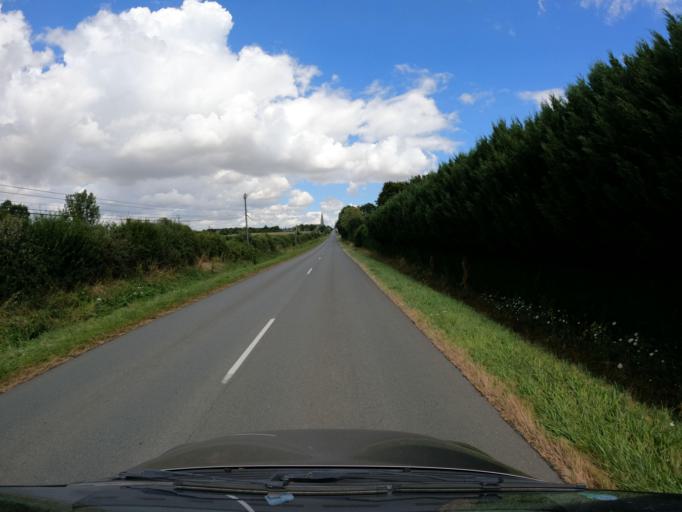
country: FR
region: Pays de la Loire
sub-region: Departement de Maine-et-Loire
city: Mire
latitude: 47.7242
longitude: -0.5220
